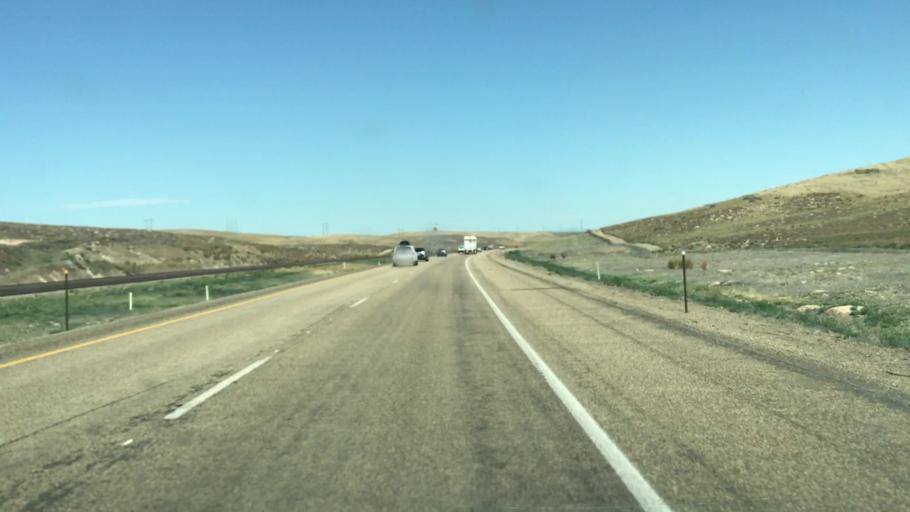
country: US
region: Idaho
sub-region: Payette County
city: New Plymouth
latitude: 43.8808
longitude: -116.7981
